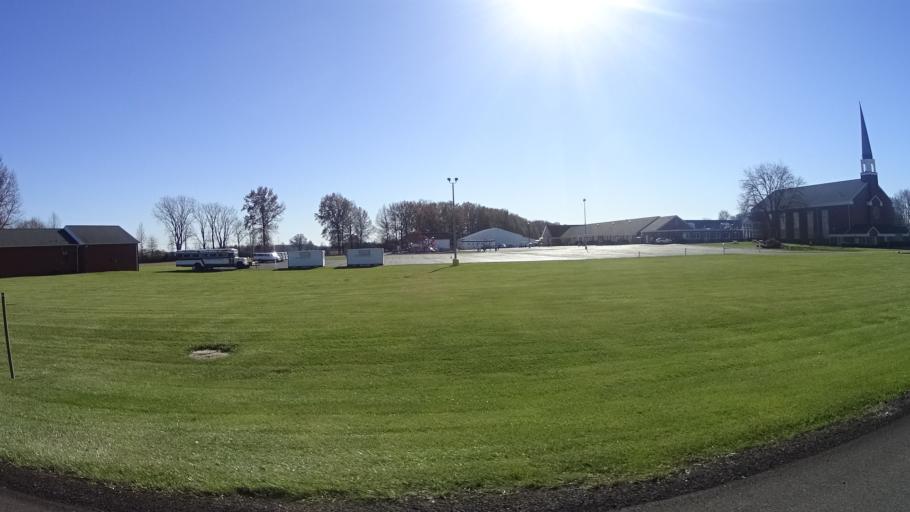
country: US
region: Ohio
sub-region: Lorain County
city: Elyria
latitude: 41.3752
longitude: -82.1602
